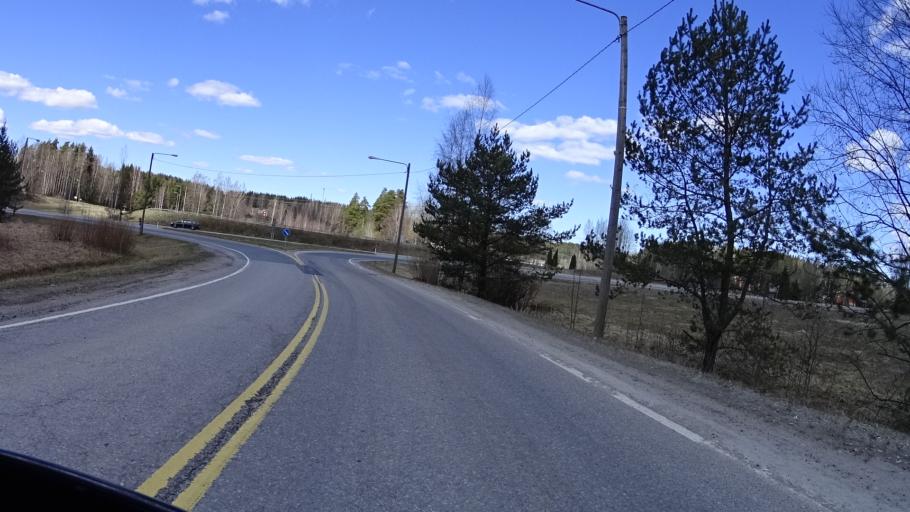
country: FI
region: Uusimaa
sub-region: Helsinki
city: Espoo
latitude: 60.2011
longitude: 24.5993
